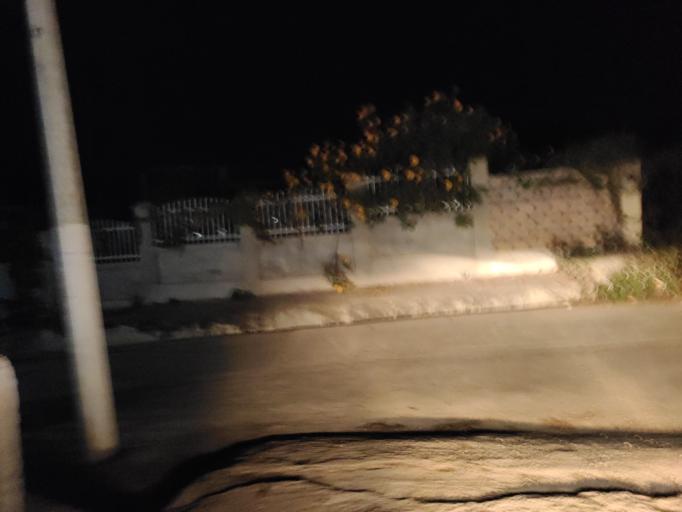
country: MM
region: Mandalay
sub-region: Pyin Oo Lwin District
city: Pyin Oo Lwin
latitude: 22.0311
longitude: 96.5038
